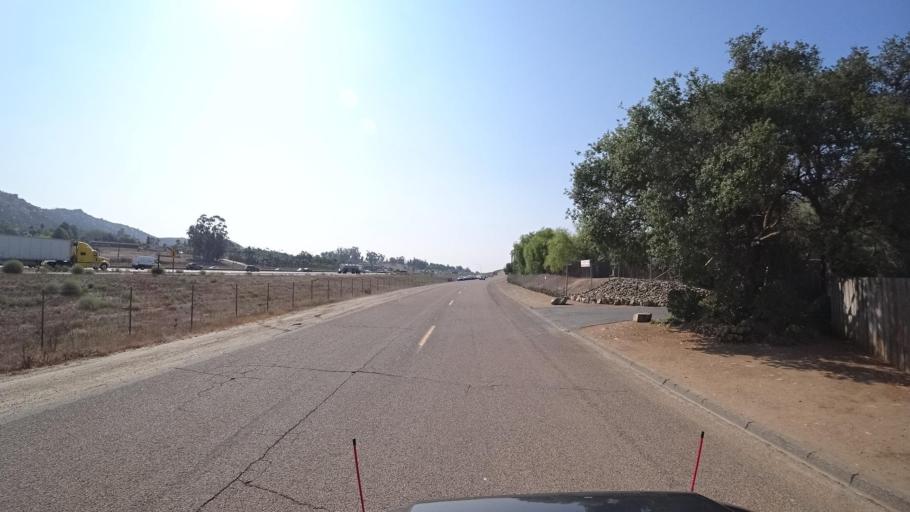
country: US
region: California
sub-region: San Diego County
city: Hidden Meadows
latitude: 33.1945
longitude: -117.1251
